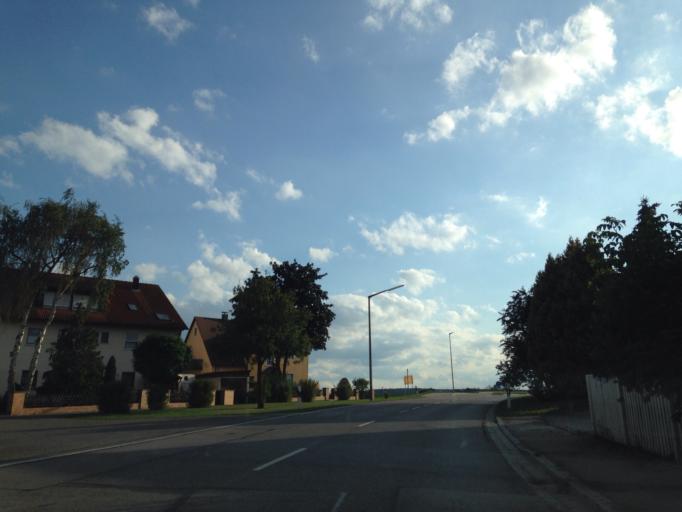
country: DE
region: Bavaria
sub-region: Upper Palatinate
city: Freystadt
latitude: 49.1679
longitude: 11.2858
